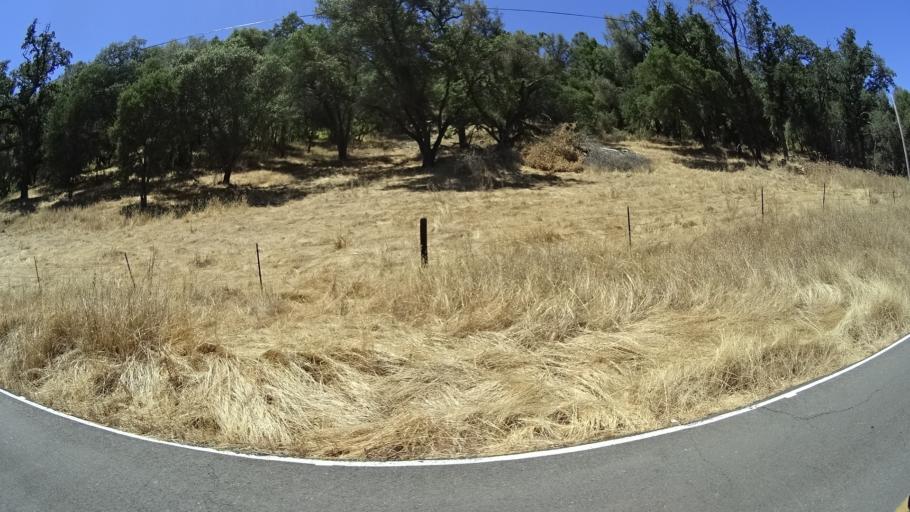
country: US
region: California
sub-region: Calaveras County
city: San Andreas
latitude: 38.1336
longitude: -120.6640
